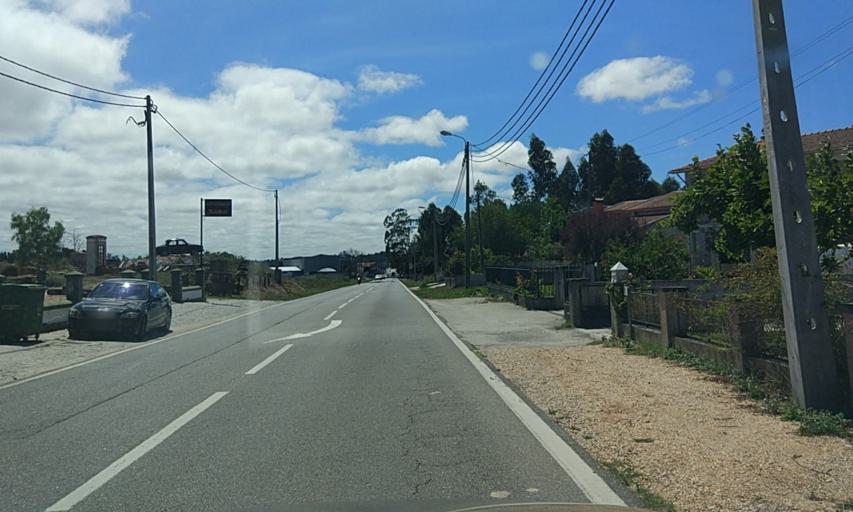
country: PT
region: Aveiro
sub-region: Vagos
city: Vagos
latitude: 40.5369
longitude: -8.6768
